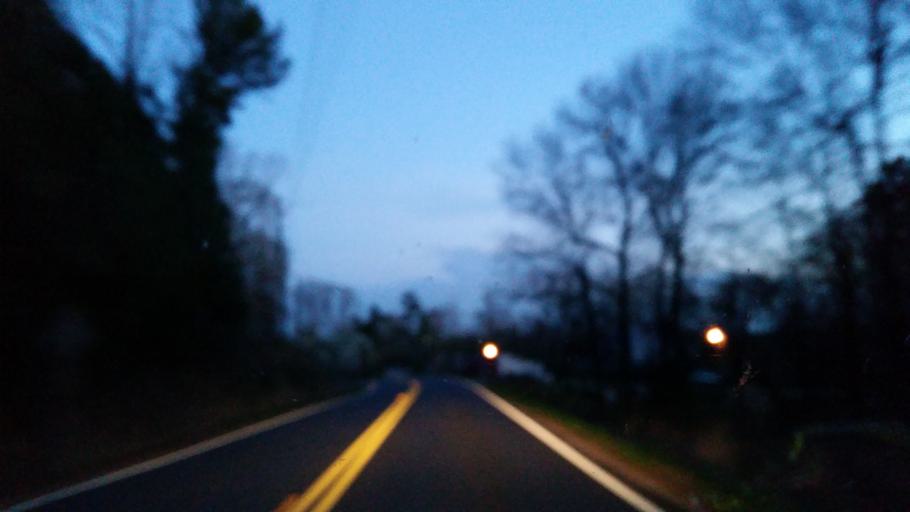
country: US
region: Georgia
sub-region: Cherokee County
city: Ball Ground
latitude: 34.2983
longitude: -84.4433
